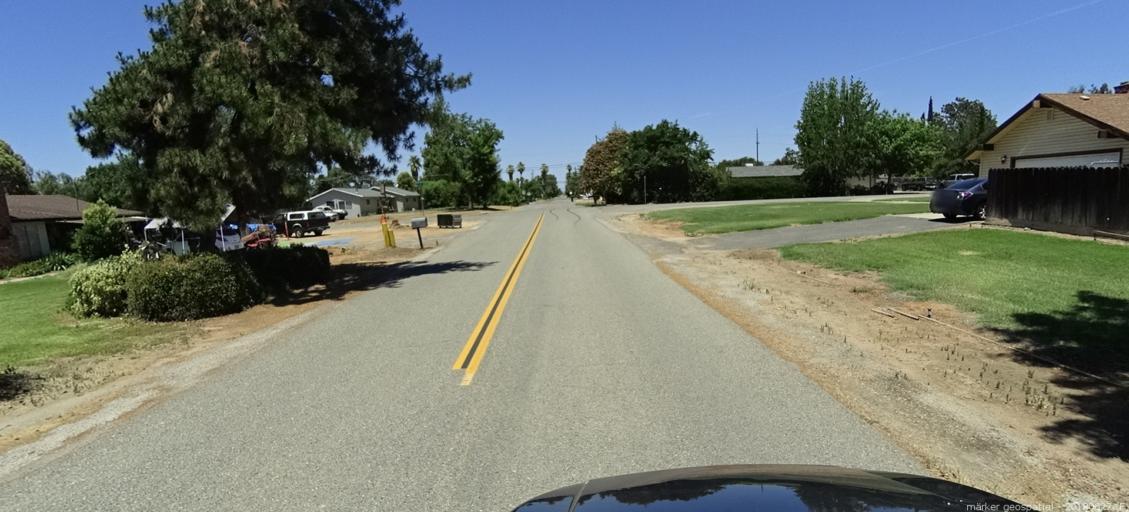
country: US
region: California
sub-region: Madera County
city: Bonadelle Ranchos-Madera Ranchos
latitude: 36.9216
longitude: -119.8912
